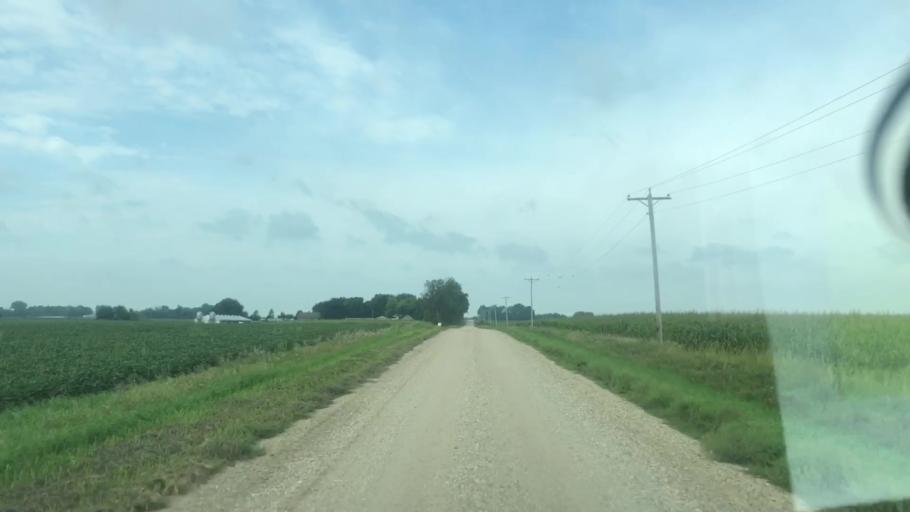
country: US
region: Iowa
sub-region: Lyon County
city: George
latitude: 43.2723
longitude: -95.9435
